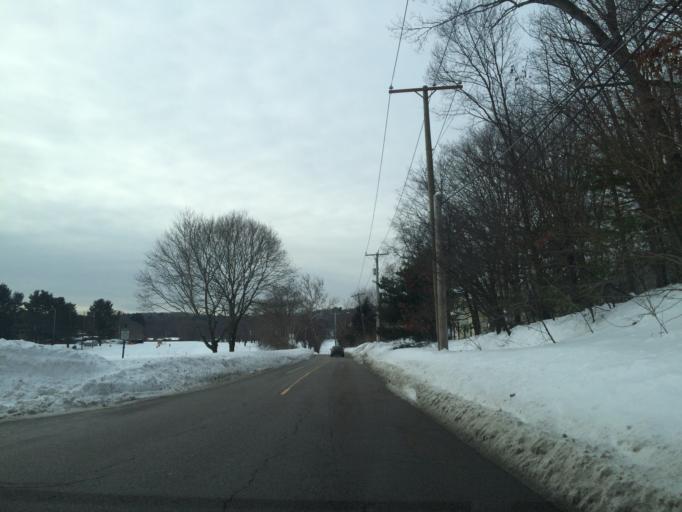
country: US
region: Massachusetts
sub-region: Norfolk County
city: Wellesley
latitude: 42.3356
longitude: -71.2680
